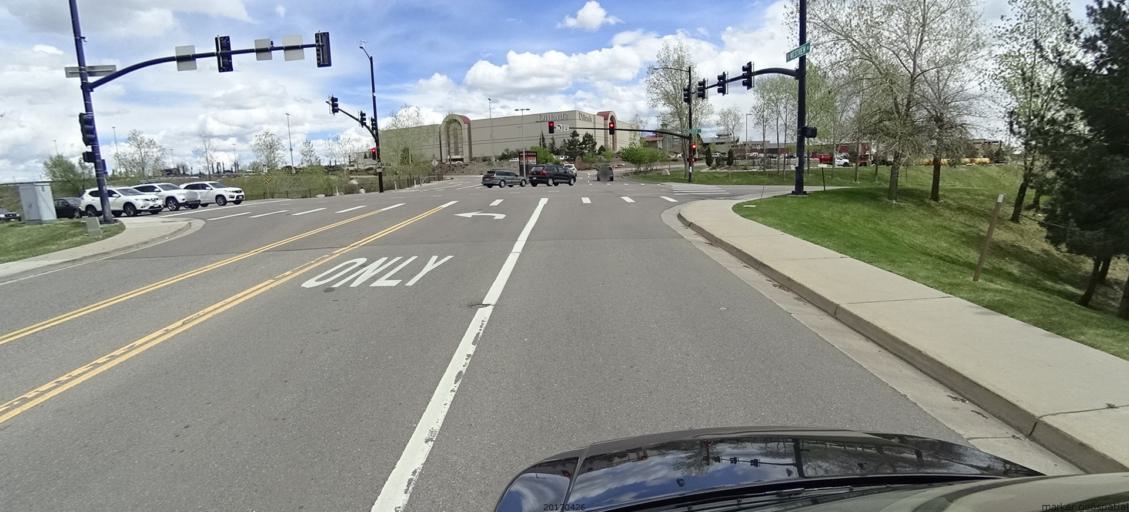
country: US
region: Colorado
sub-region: Adams County
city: Lone Tree
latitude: 39.5646
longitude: -104.8812
